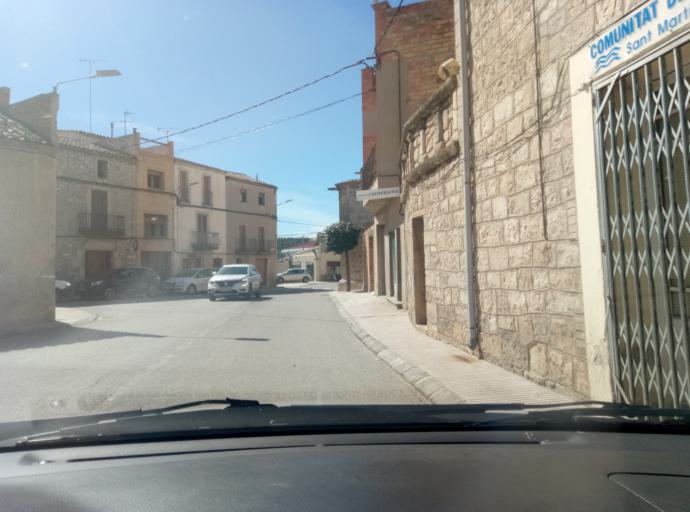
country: ES
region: Catalonia
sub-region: Provincia de Lleida
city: Vallbona de les Monges
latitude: 41.5597
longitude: 1.0551
